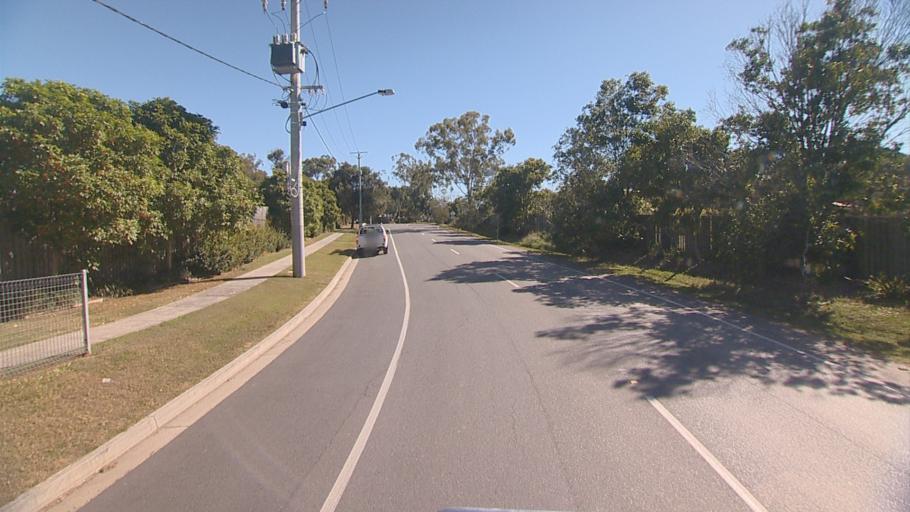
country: AU
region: Queensland
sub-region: Logan
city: Woodridge
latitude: -27.6516
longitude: 153.0682
